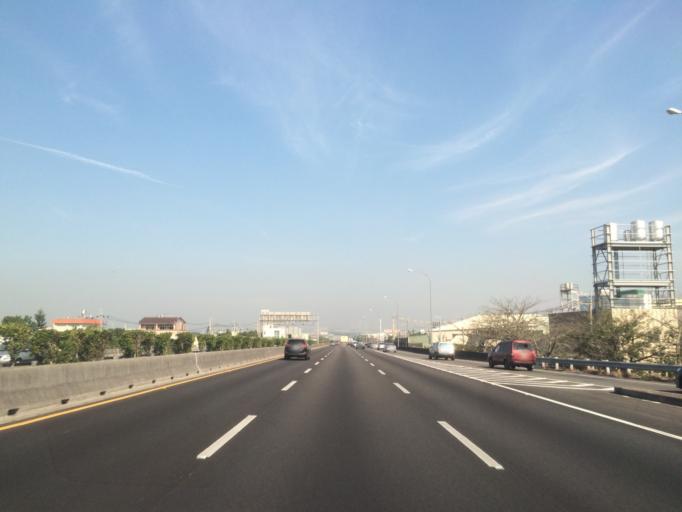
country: TW
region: Taiwan
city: Fengyuan
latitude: 24.2529
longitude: 120.6907
